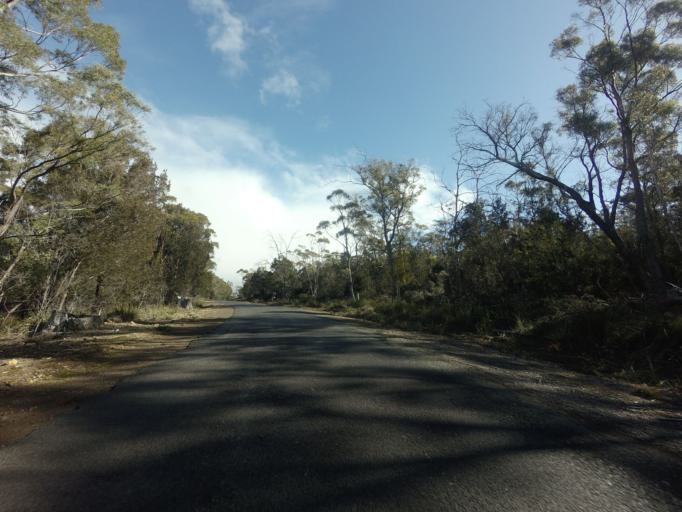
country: AU
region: Tasmania
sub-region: Sorell
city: Sorell
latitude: -42.3598
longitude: 147.9576
